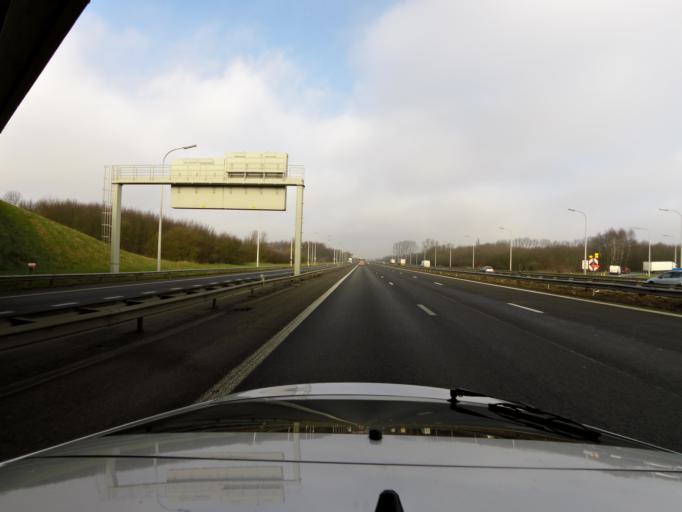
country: BE
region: Flanders
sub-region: Provincie West-Vlaanderen
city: Wevelgem
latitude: 50.8302
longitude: 3.1873
